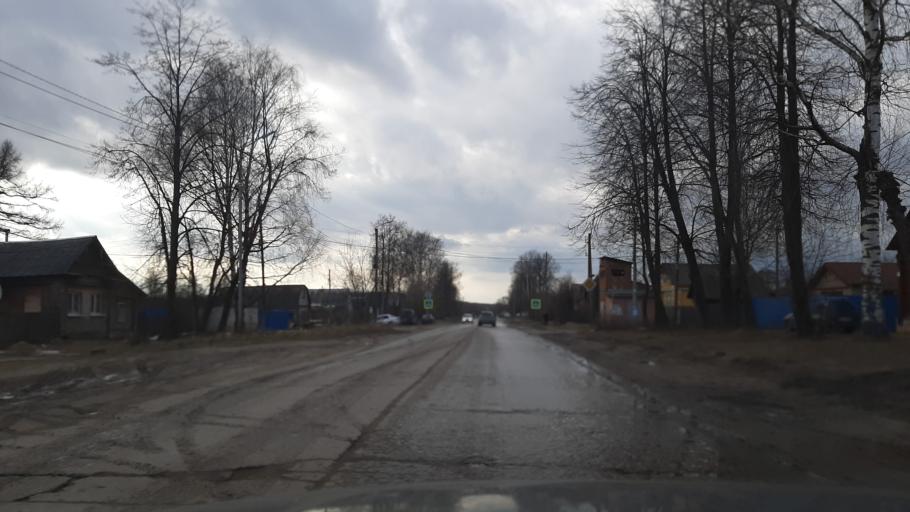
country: RU
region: Ivanovo
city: Teykovo
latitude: 56.8593
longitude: 40.5287
